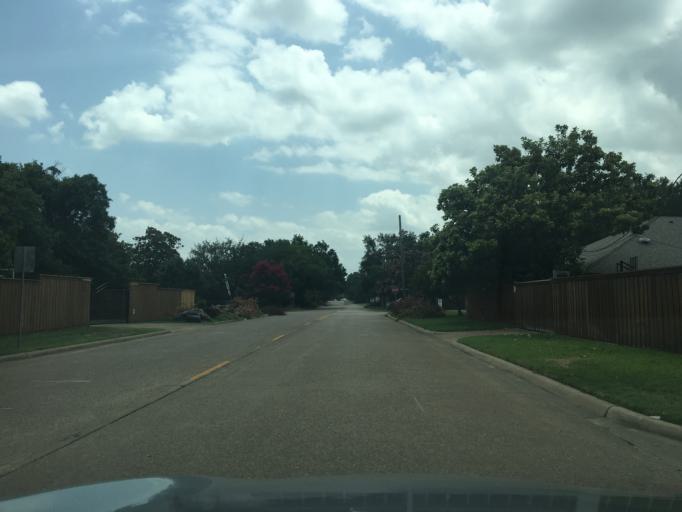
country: US
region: Texas
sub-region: Dallas County
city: Addison
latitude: 32.9029
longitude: -96.8297
